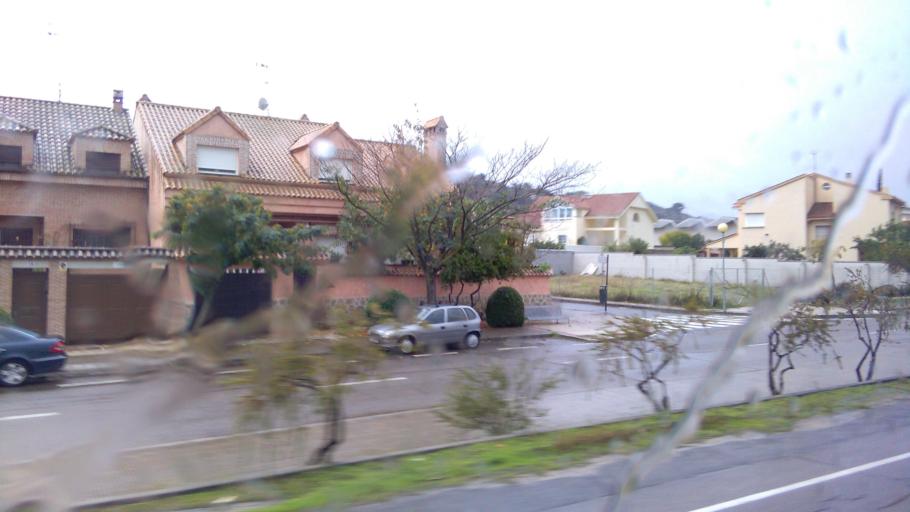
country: ES
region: Extremadura
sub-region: Provincia de Caceres
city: Navalmoral de la Mata
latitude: 39.8914
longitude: -5.5263
